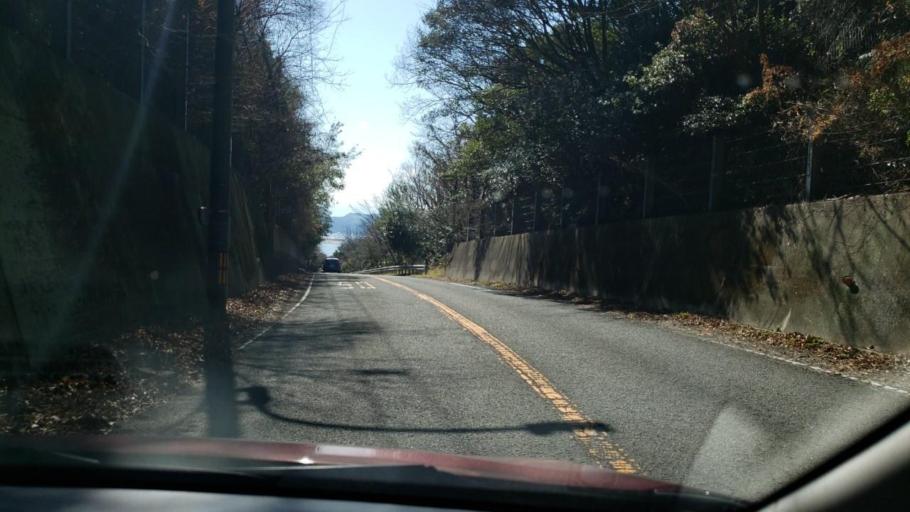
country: JP
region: Tokushima
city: Narutocho-mitsuishi
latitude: 34.2374
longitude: 134.6061
